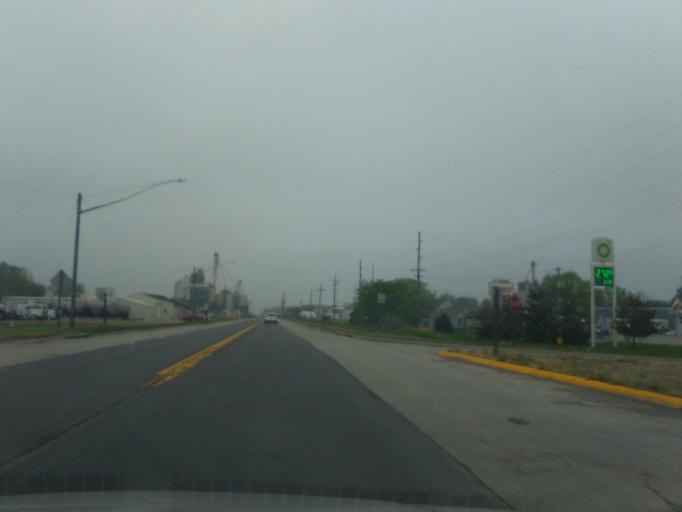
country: US
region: Nebraska
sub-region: Cuming County
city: Wisner
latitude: 41.9258
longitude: -96.8069
